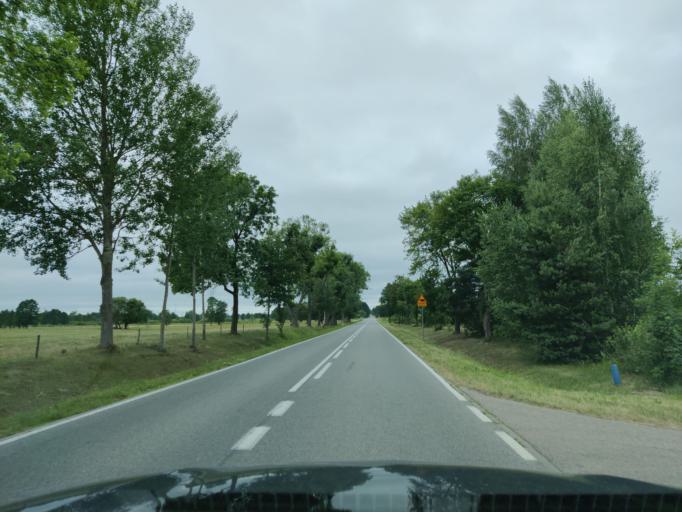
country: PL
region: Masovian Voivodeship
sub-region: Powiat ostrolecki
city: Czarnia
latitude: 53.3253
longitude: 21.1675
